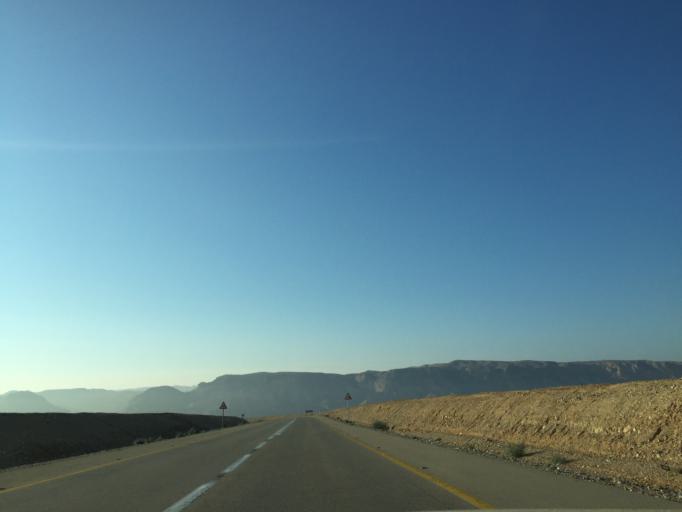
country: IL
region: Southern District
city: Mitzpe Ramon
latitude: 30.3387
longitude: 34.9492
